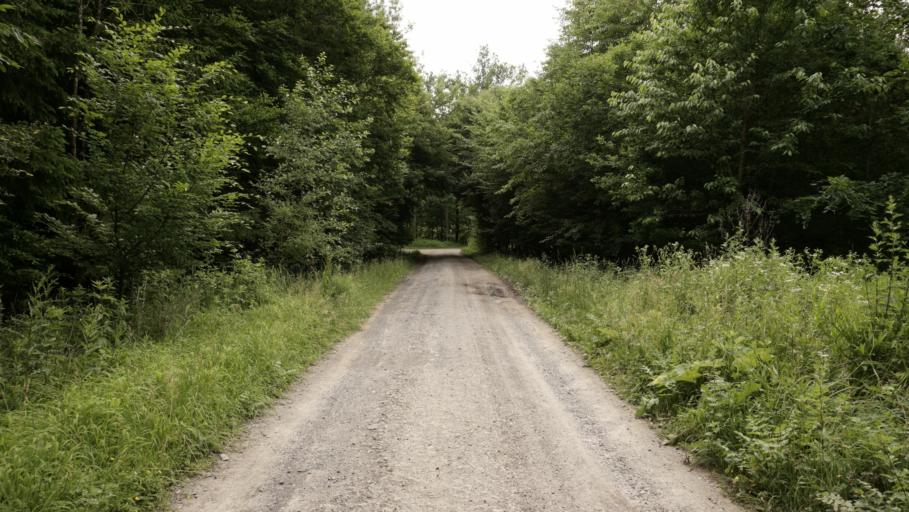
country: DE
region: Baden-Wuerttemberg
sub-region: Karlsruhe Region
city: Mosbach
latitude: 49.3276
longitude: 9.1919
